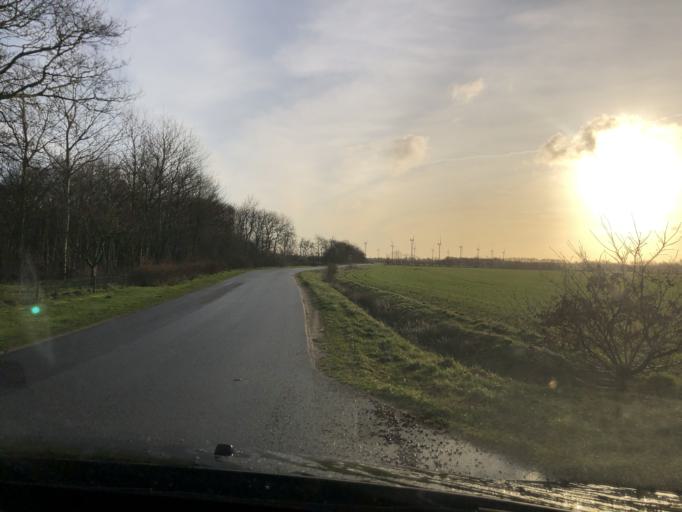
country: DK
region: Central Jutland
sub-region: Ringkobing-Skjern Kommune
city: Skjern
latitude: 55.8618
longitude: 8.3773
